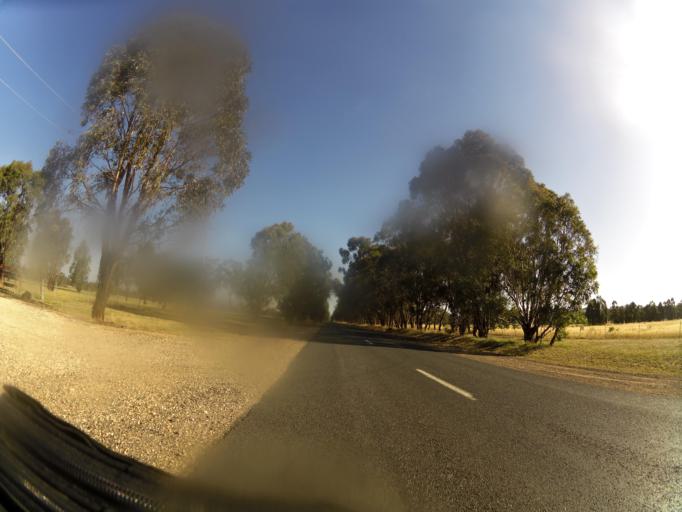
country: AU
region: Victoria
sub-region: Murrindindi
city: Kinglake West
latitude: -36.9876
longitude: 145.1118
